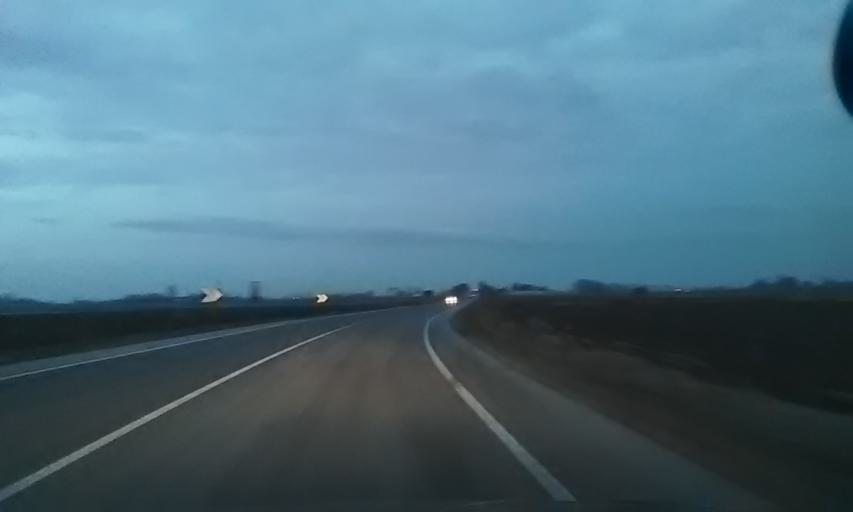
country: IT
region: Piedmont
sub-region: Provincia di Vercelli
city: Stroppiana
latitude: 45.2394
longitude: 8.4573
